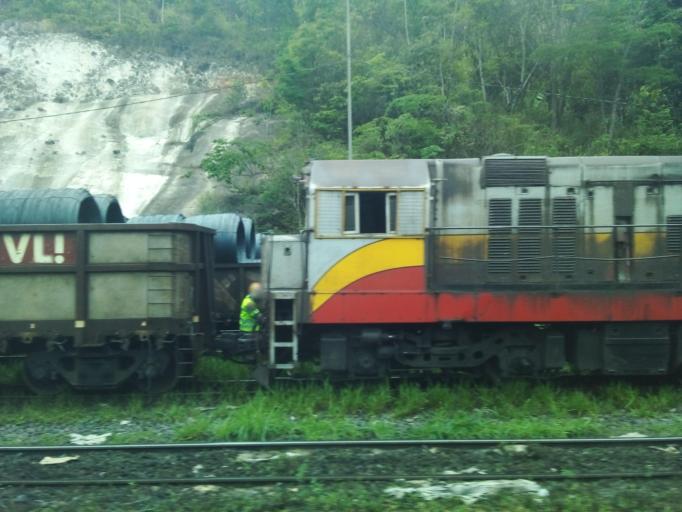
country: BR
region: Minas Gerais
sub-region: Joao Monlevade
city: Joao Monlevade
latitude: -19.8409
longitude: -43.1291
